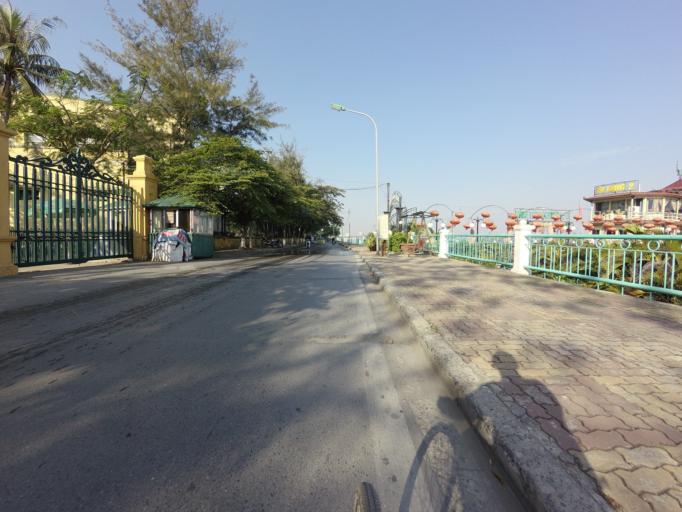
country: VN
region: Ha Noi
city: Hanoi
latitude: 21.0437
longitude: 105.8330
